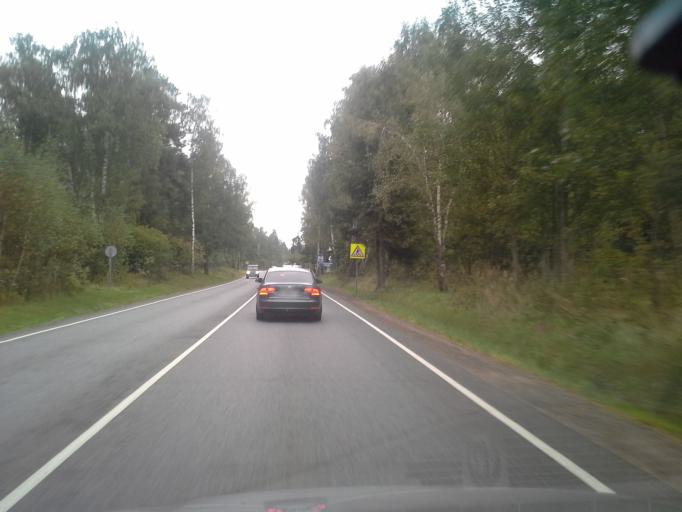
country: RU
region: Moskovskaya
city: Zhavoronki
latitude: 55.7066
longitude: 37.0958
